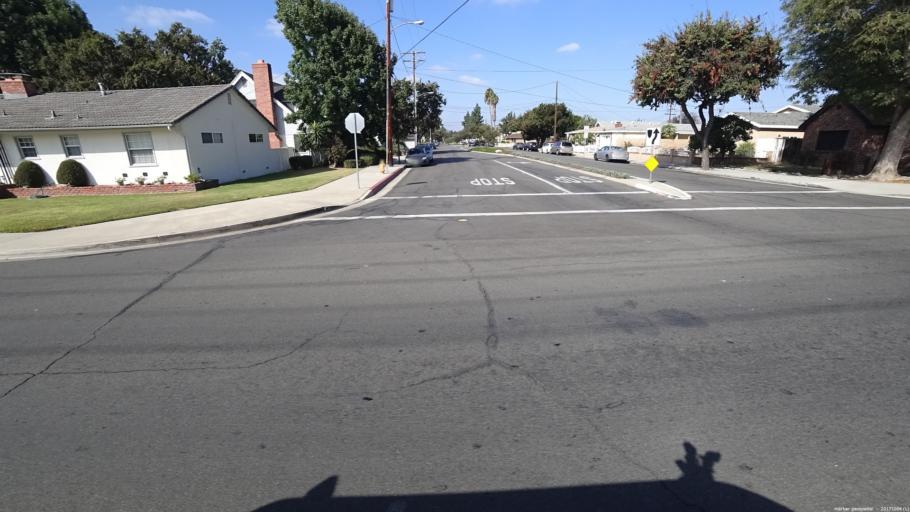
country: US
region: California
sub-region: Orange County
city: Garden Grove
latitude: 33.7777
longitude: -117.9323
